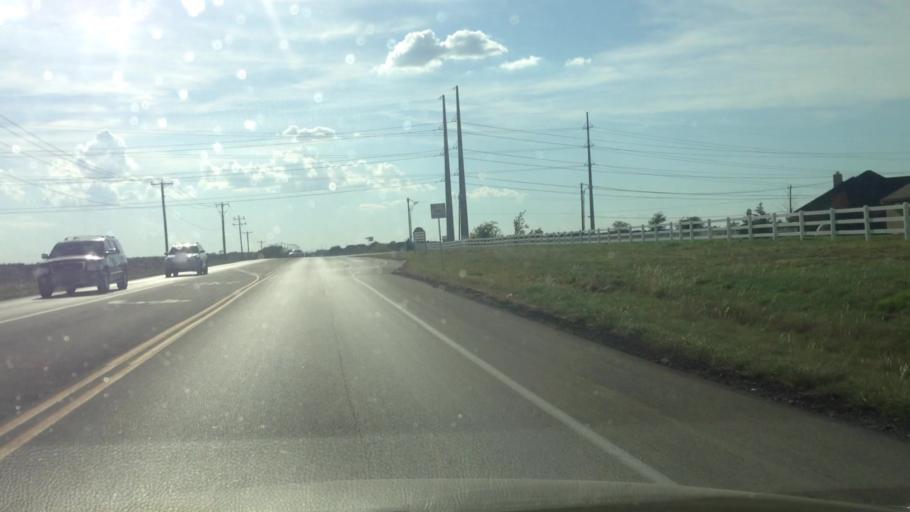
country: US
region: Texas
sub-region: Tarrant County
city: Eagle Mountain
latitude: 32.9245
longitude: -97.3900
